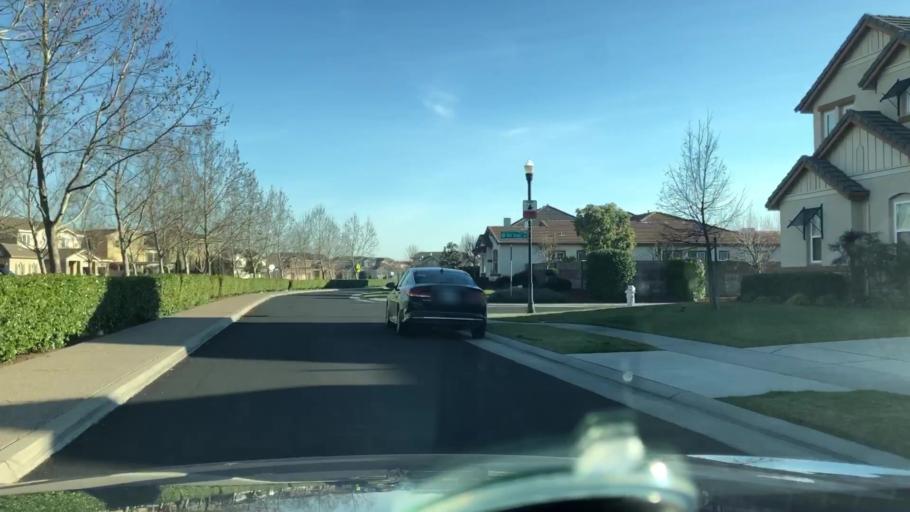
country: US
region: California
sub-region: Sacramento County
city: Laguna
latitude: 38.3986
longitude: -121.4044
